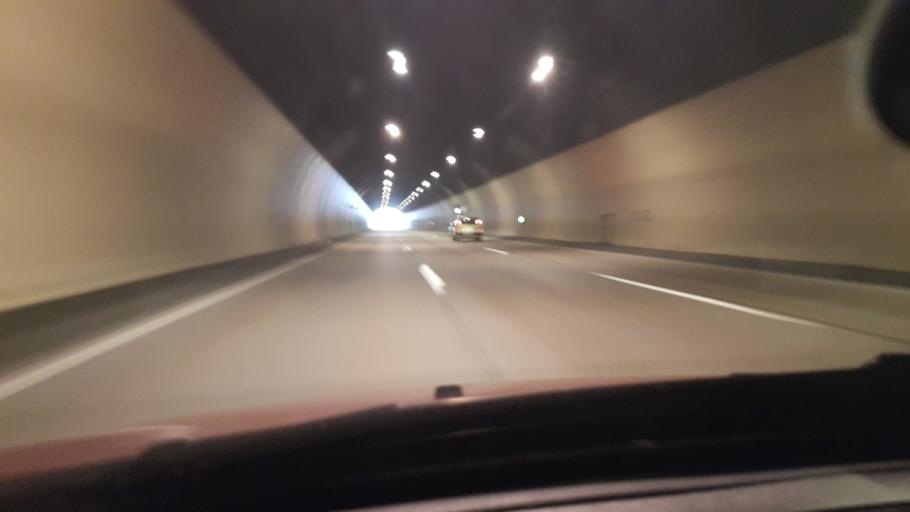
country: AT
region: Styria
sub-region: Politischer Bezirk Graz-Umgebung
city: Gratkorn
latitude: 47.1262
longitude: 15.3649
